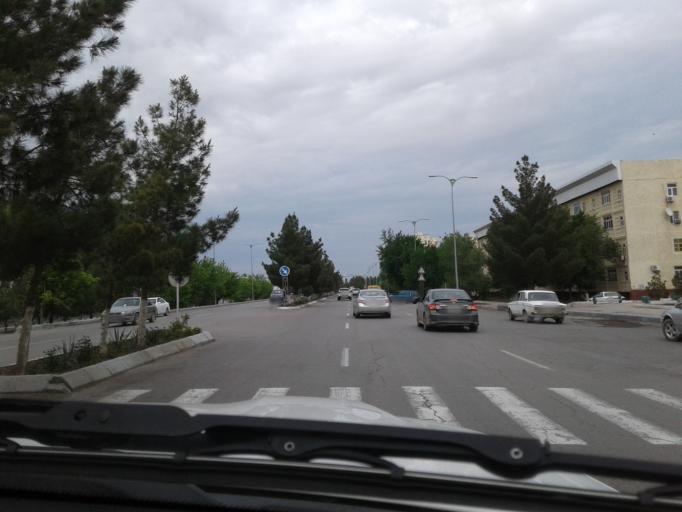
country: TM
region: Mary
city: Mary
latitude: 37.5922
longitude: 61.8723
